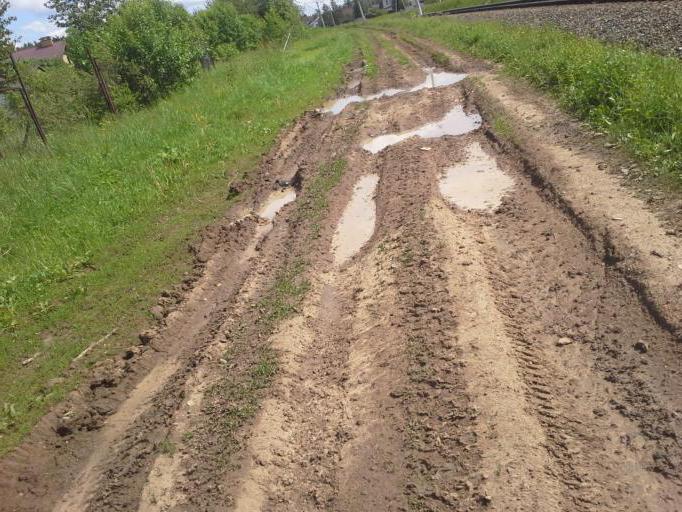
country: RU
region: Moscow
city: Tolstopal'tsevo
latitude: 55.6237
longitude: 37.2210
